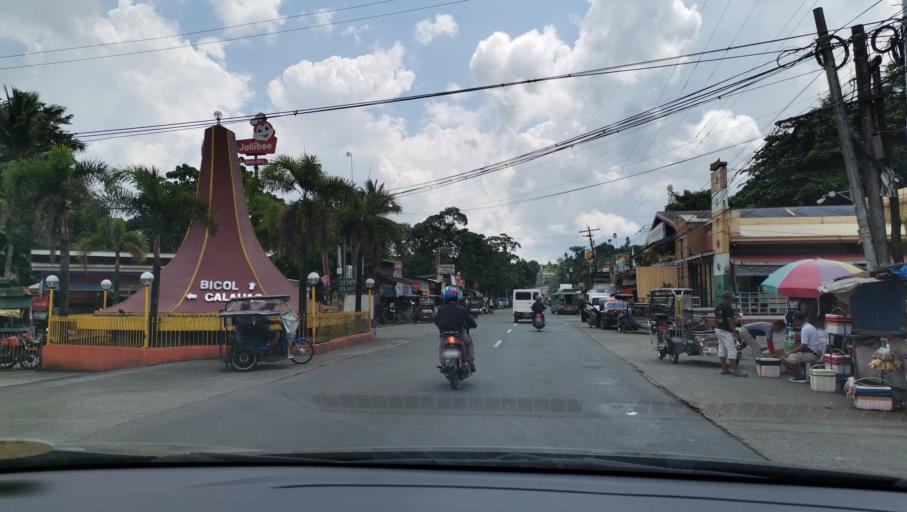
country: PH
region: Calabarzon
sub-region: Province of Quezon
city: Calauag
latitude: 13.9531
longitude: 122.2970
